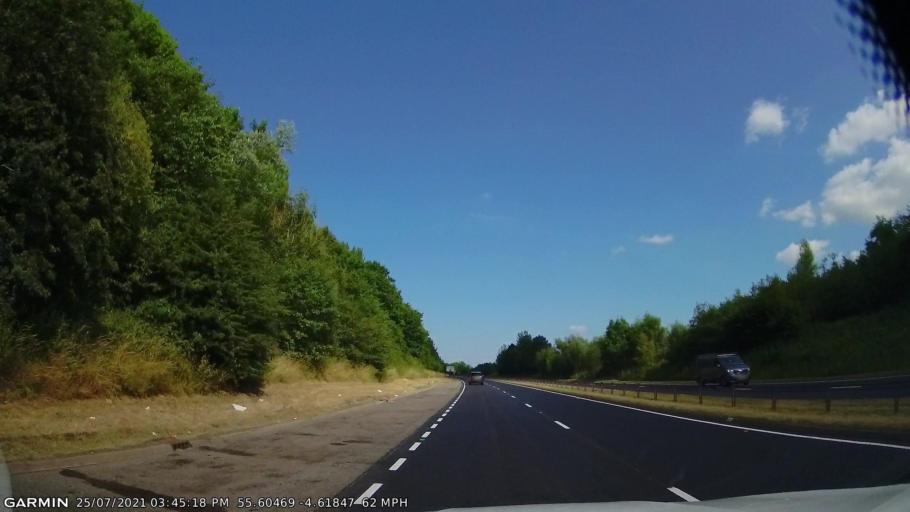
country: GB
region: Scotland
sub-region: North Ayrshire
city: Dreghorn
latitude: 55.6047
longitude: -4.6194
